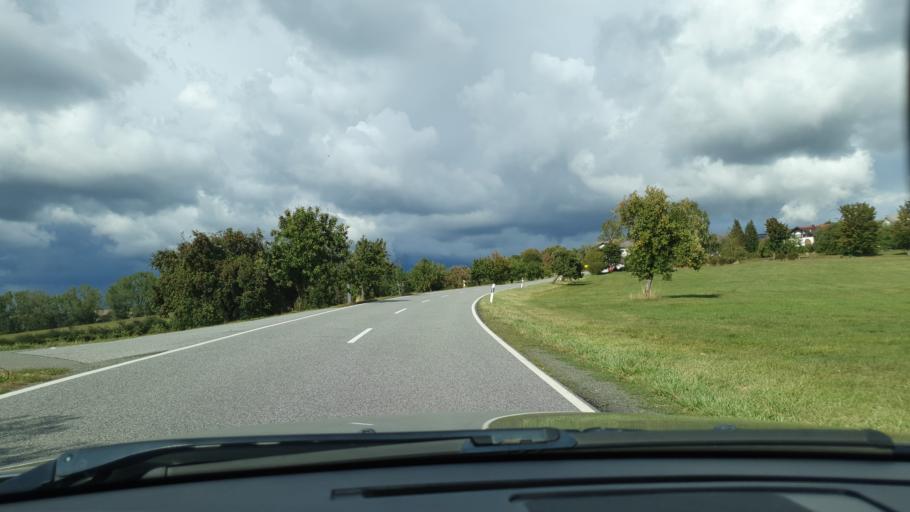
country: DE
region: Rheinland-Pfalz
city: Wallhalben
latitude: 49.3207
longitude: 7.5413
